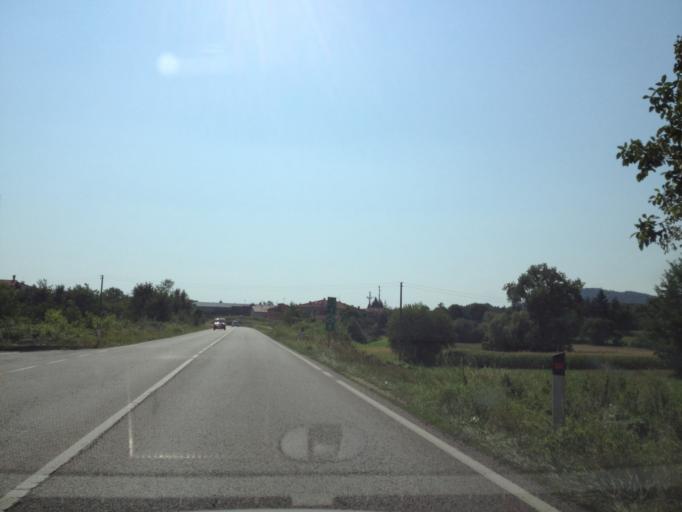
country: IT
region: Veneto
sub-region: Provincia di Vicenza
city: Cogollo del Cengio
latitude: 45.7888
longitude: 11.4117
